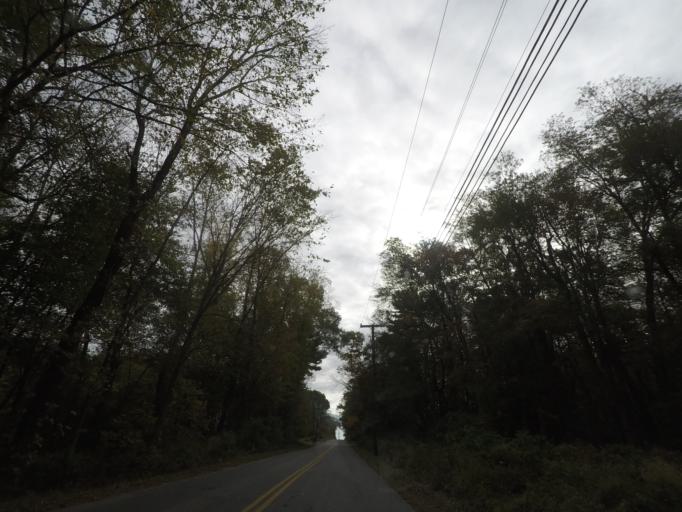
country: US
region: Connecticut
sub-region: Windham County
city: Thompson
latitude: 41.9537
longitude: -71.8507
